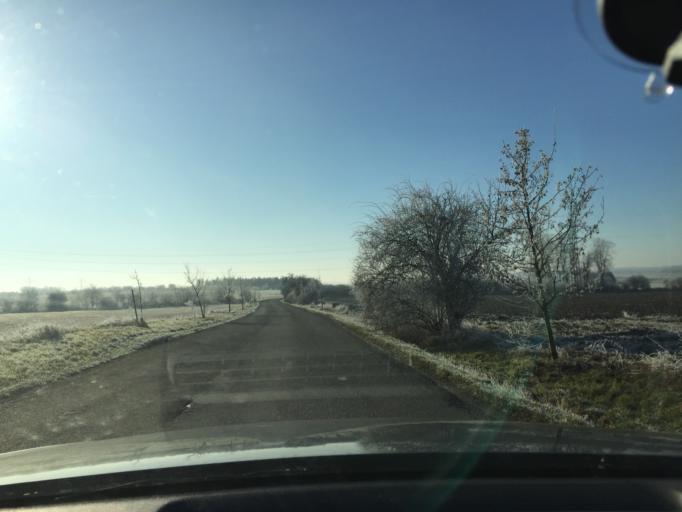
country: CZ
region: Central Bohemia
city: Trebotov
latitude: 50.0090
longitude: 14.2827
